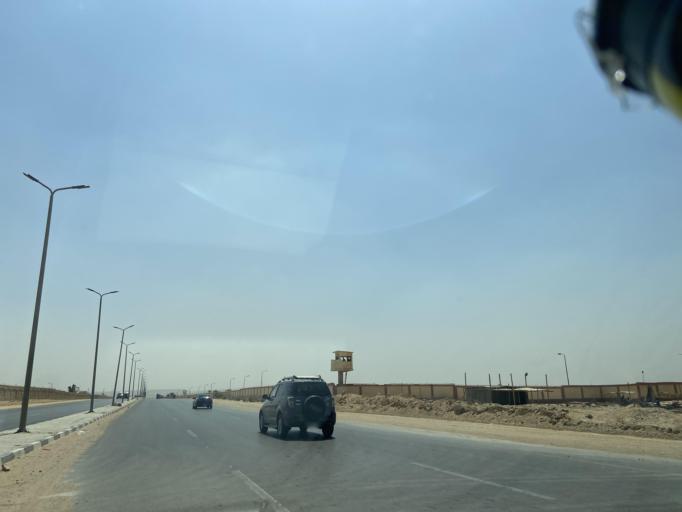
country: EG
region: Muhafazat al Qahirah
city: Cairo
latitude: 30.0011
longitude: 31.3518
